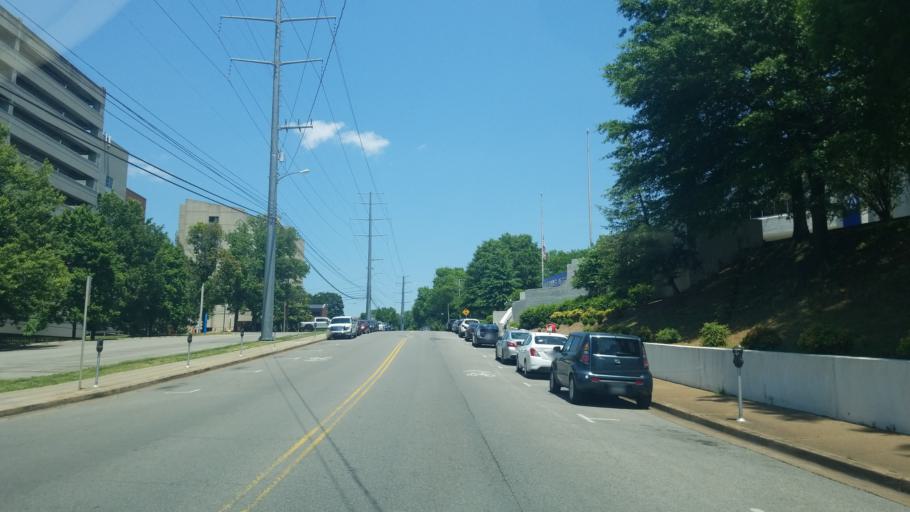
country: US
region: Tennessee
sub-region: Davidson County
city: Nashville
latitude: 36.1412
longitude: -86.8050
